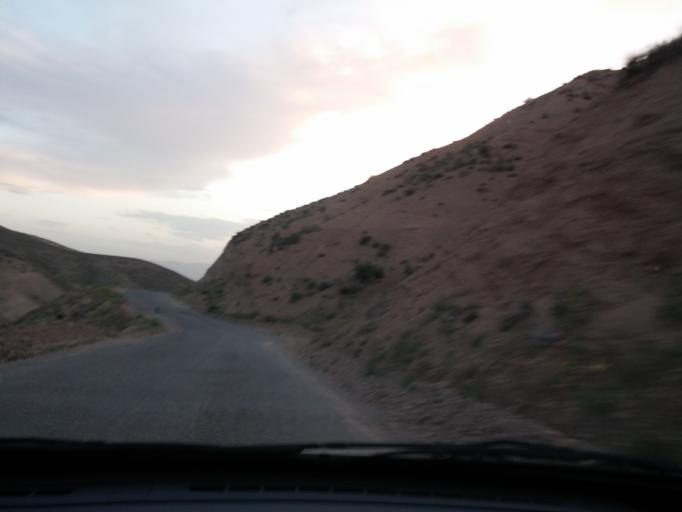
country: IR
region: Semnan
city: Istgah-e Rah Ahan-e Garmsar
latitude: 35.5348
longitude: 52.3125
